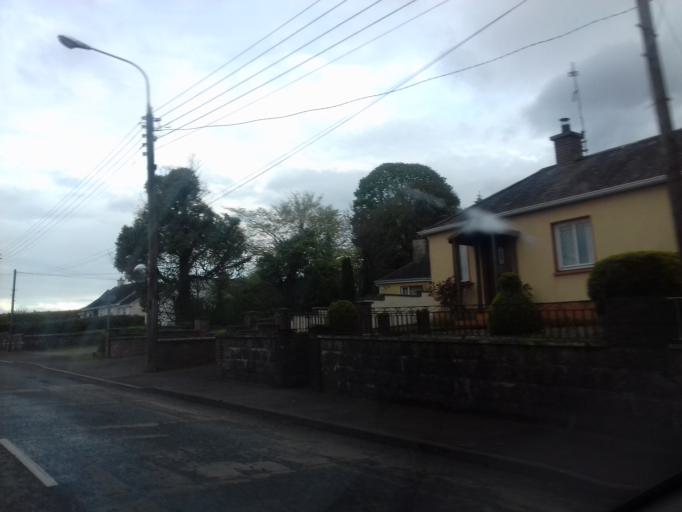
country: IE
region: Ulster
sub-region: An Cabhan
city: Ballyconnell
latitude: 54.1138
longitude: -7.5804
